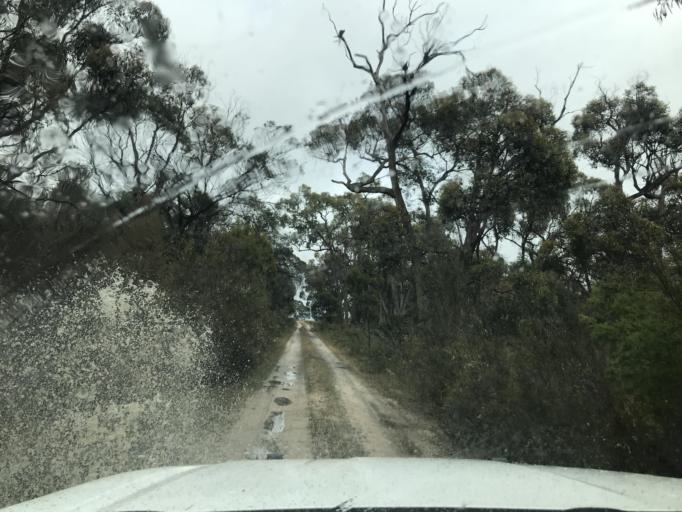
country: AU
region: South Australia
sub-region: Wattle Range
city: Penola
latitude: -37.2638
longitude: 141.3052
